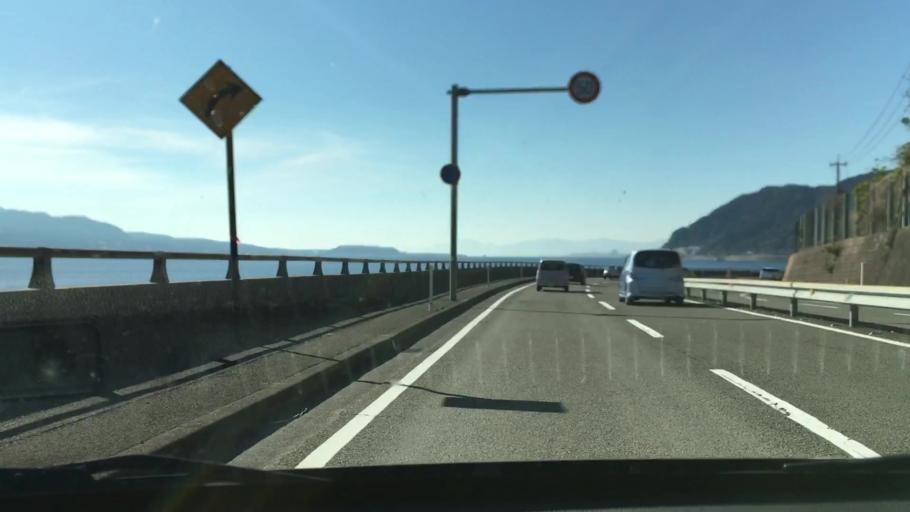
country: JP
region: Kagoshima
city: Kajiki
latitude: 31.6572
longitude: 130.6190
